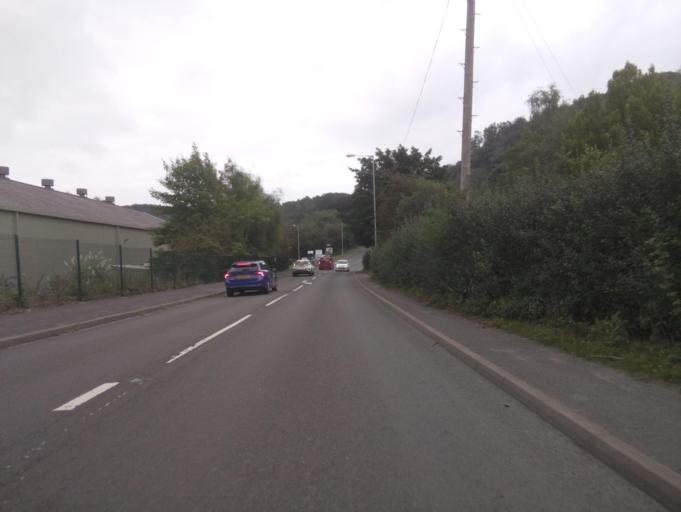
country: GB
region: England
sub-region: Staffordshire
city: Cheadle
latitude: 53.0224
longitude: -1.9643
